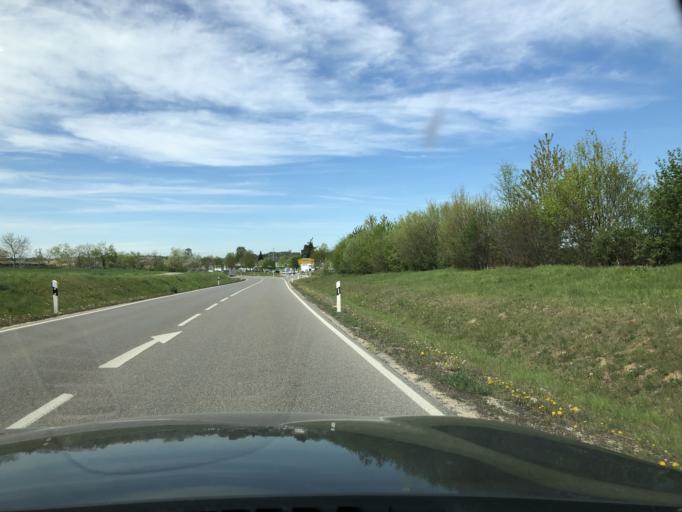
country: DE
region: Bavaria
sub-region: Swabia
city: Laugna
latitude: 48.5532
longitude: 10.6990
